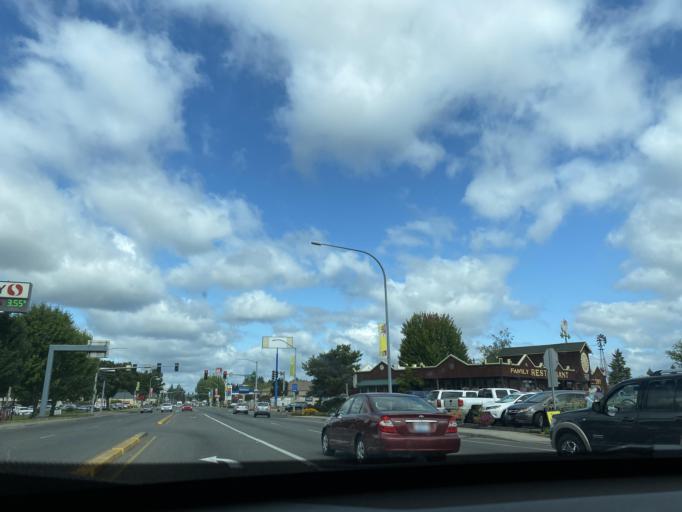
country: US
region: Washington
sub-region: Lewis County
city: Fords Prairie
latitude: 46.7280
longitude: -122.9787
